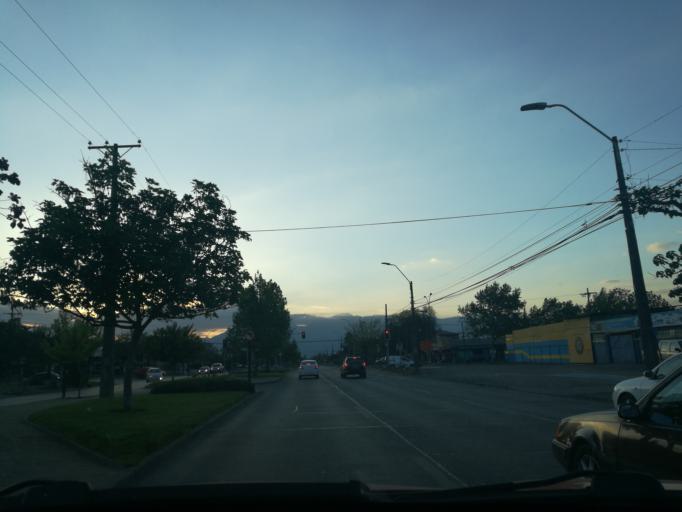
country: CL
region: O'Higgins
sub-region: Provincia de Cachapoal
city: Rancagua
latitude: -34.1558
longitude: -70.7312
